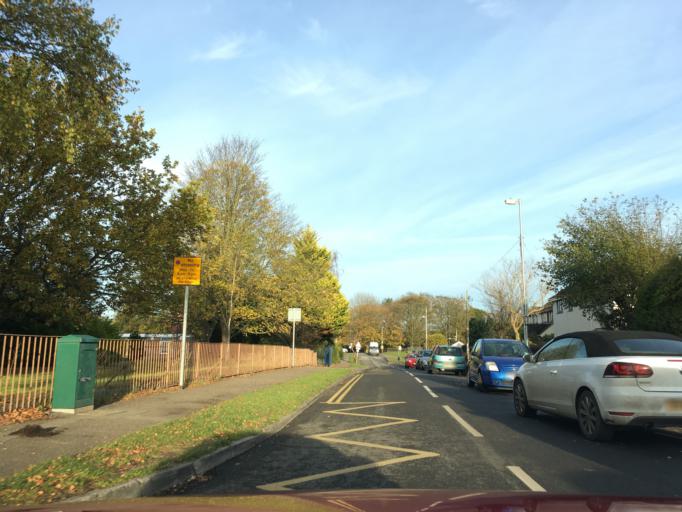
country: GB
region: England
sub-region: South Gloucestershire
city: Thornbury
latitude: 51.6151
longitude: -2.5237
